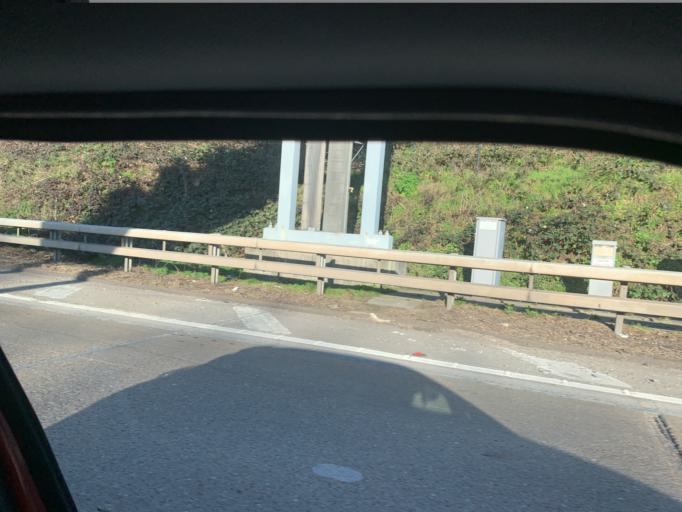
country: GB
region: England
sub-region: Surrey
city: Addlestone
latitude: 51.3686
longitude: -0.5055
